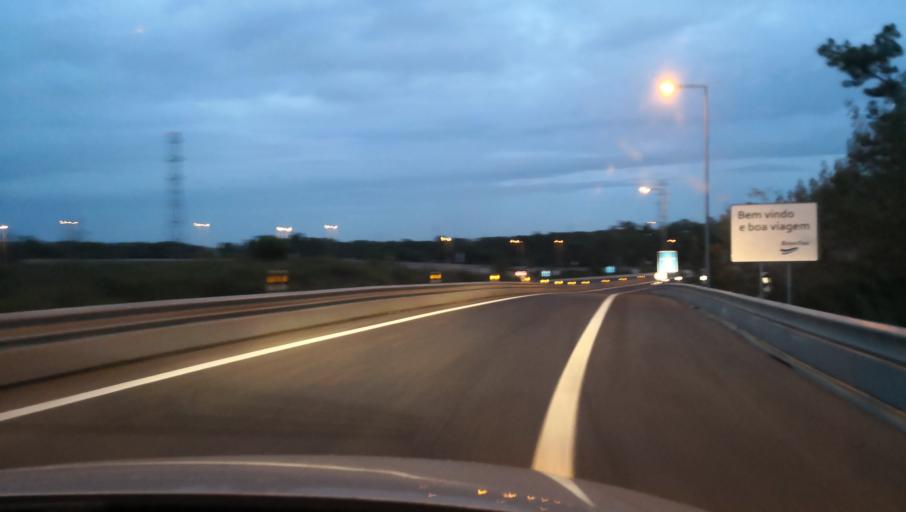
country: PT
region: Setubal
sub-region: Seixal
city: Amora
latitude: 38.6014
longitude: -9.1306
